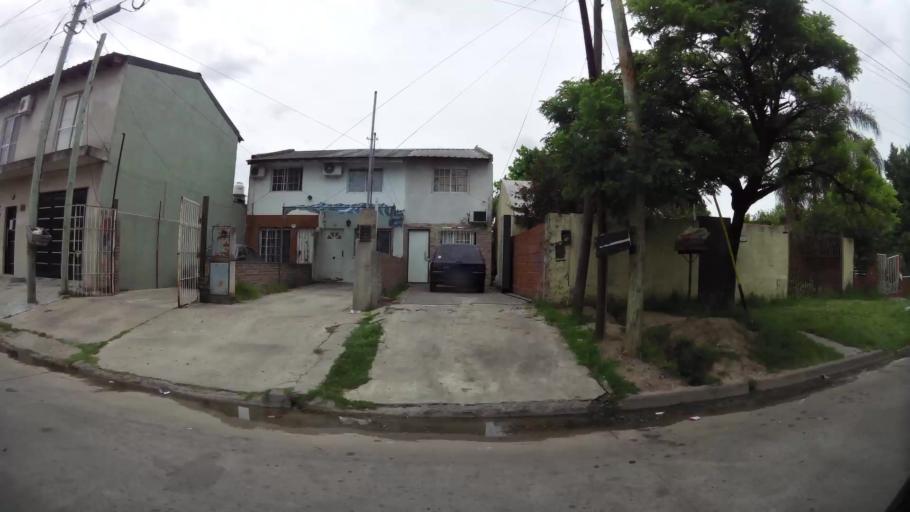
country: AR
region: Buenos Aires
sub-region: Partido de Campana
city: Campana
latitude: -34.1789
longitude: -58.9482
